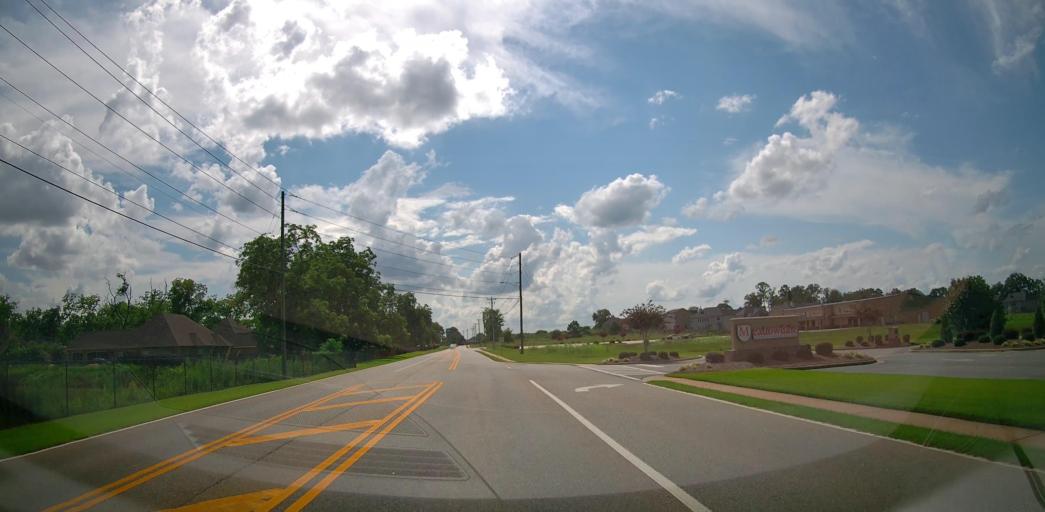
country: US
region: Georgia
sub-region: Houston County
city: Centerville
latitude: 32.5712
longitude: -83.6952
